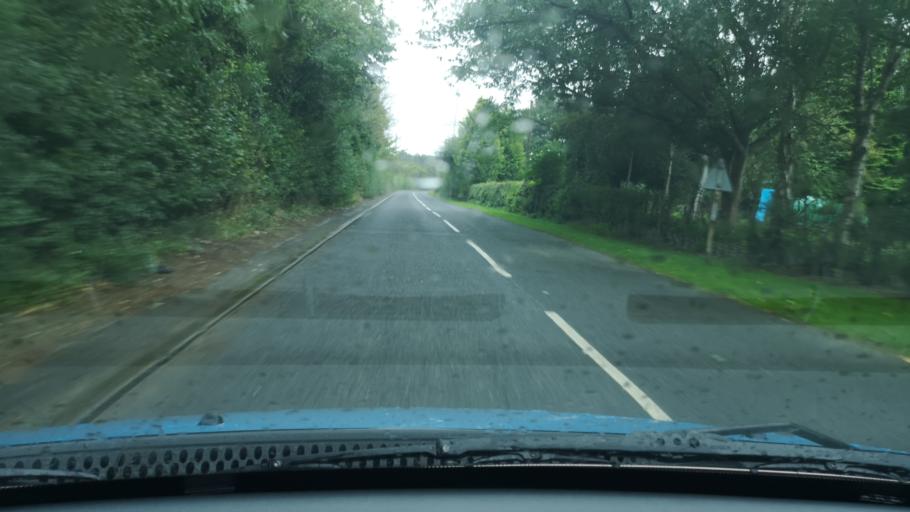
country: GB
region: England
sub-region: Doncaster
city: Norton
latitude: 53.6756
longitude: -1.2097
